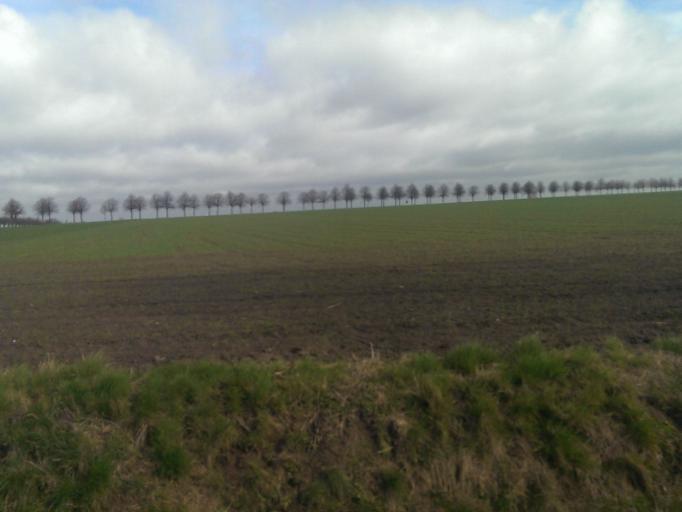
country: DE
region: Lower Saxony
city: Schellerten
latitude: 52.1705
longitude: 10.0460
